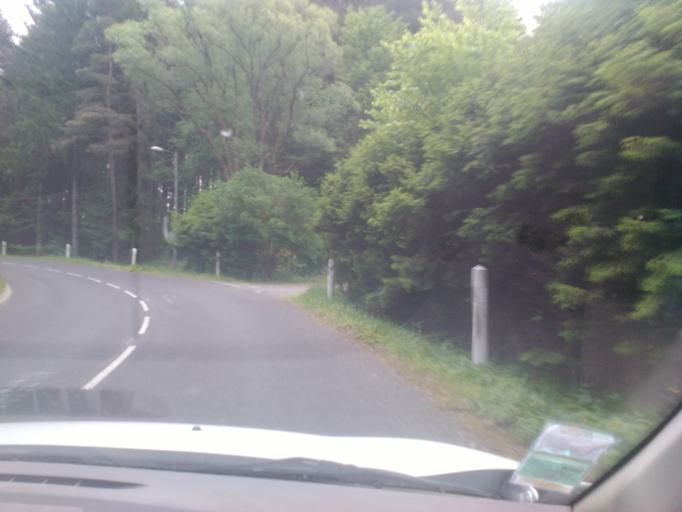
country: FR
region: Lorraine
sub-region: Departement des Vosges
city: Etival-Clairefontaine
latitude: 48.3601
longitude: 6.8248
